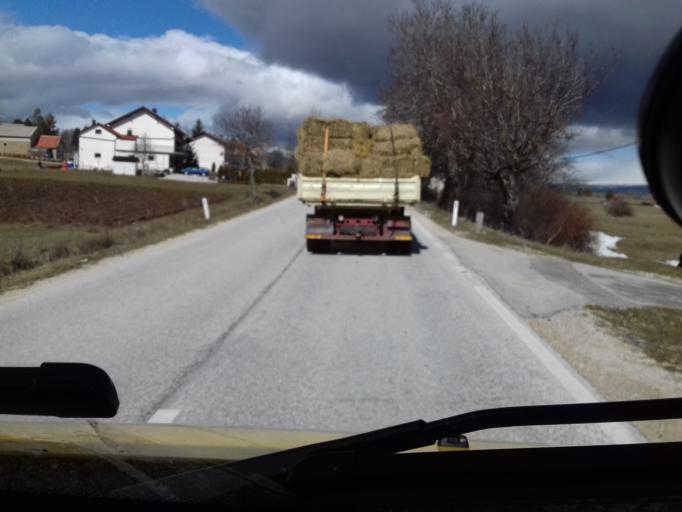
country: BA
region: Federation of Bosnia and Herzegovina
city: Dreznica
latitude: 43.6037
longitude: 17.2729
